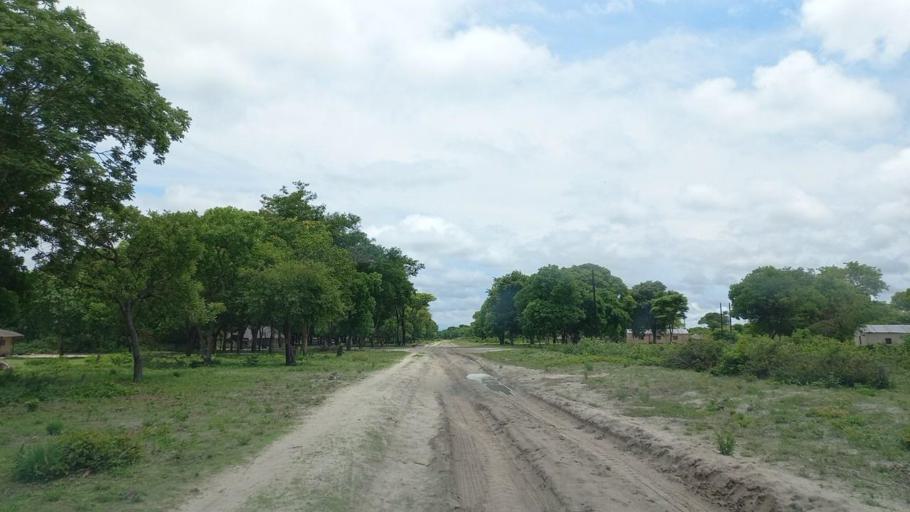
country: ZM
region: North-Western
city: Kabompo
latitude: -13.1866
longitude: 23.9557
